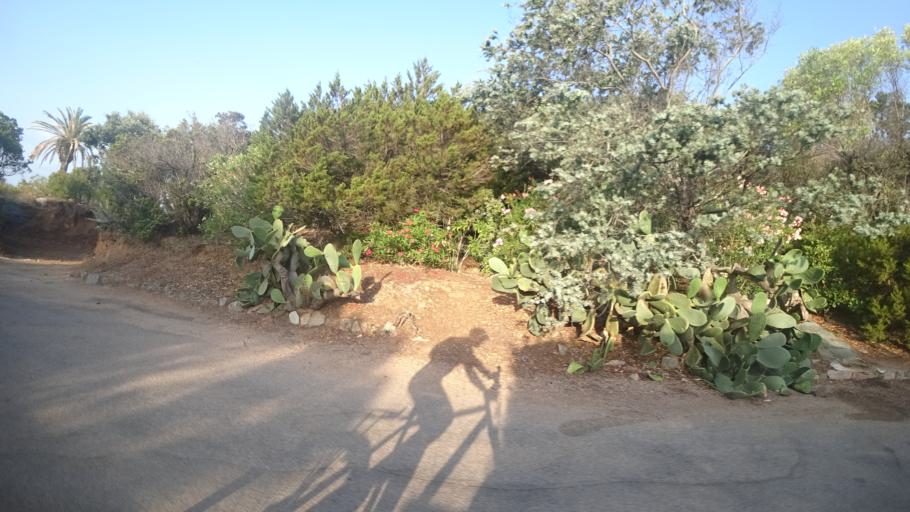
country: FR
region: Corsica
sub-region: Departement de la Corse-du-Sud
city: Porto-Vecchio
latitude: 41.6212
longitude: 9.3529
